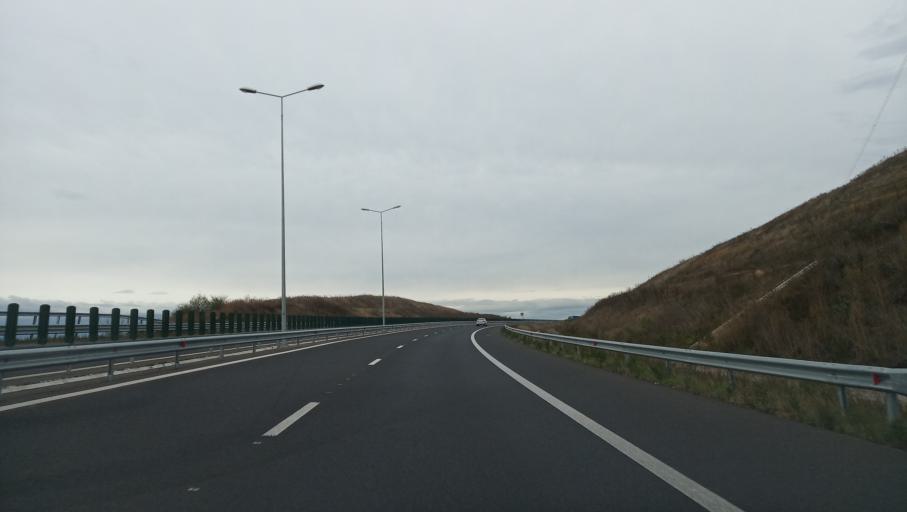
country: RO
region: Hunedoara
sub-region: Comuna Branisca
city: Branisca
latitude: 45.9125
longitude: 22.7864
